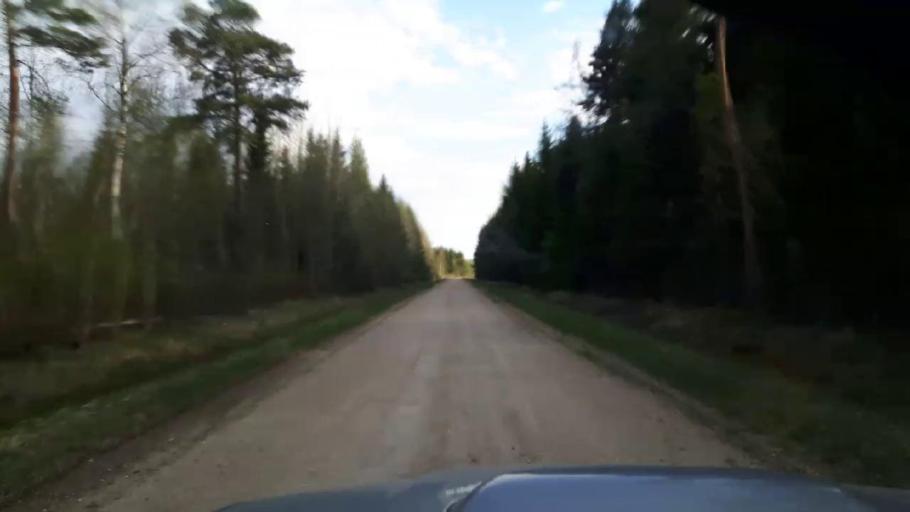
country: EE
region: Paernumaa
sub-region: Tootsi vald
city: Tootsi
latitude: 58.4497
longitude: 24.8224
